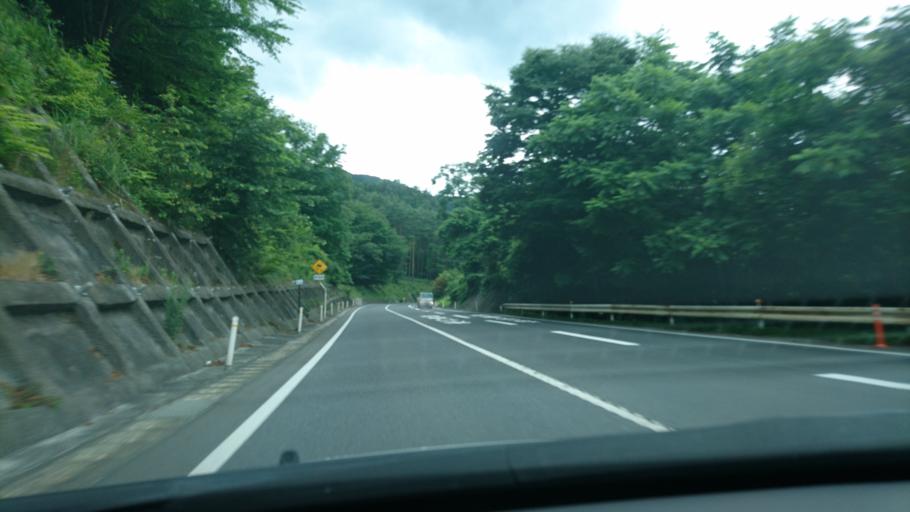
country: JP
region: Iwate
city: Kamaishi
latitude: 39.1898
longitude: 141.8481
